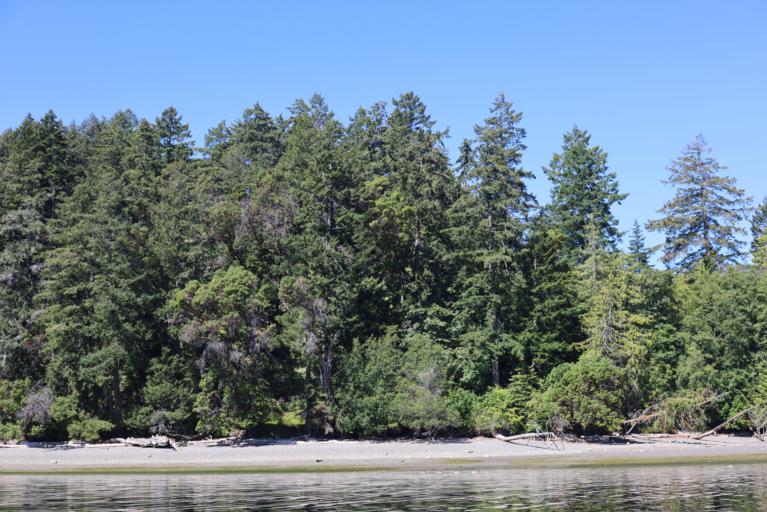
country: CA
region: British Columbia
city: North Cowichan
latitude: 48.8588
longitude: -123.6159
